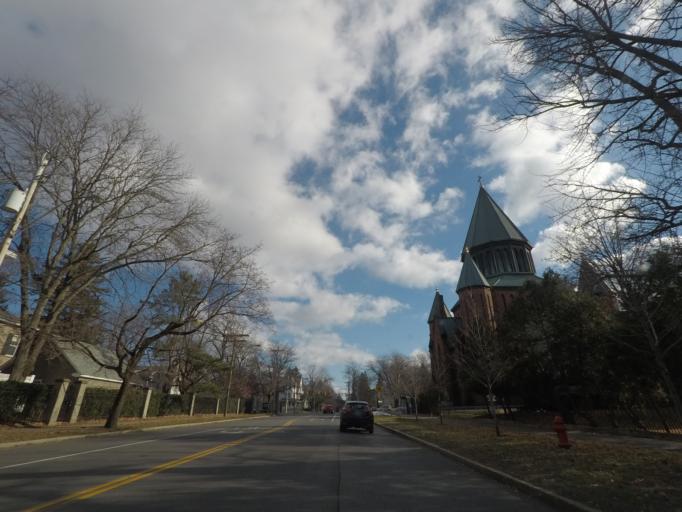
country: US
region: New York
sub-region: Schenectady County
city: Schenectady
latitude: 42.8149
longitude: -73.9326
